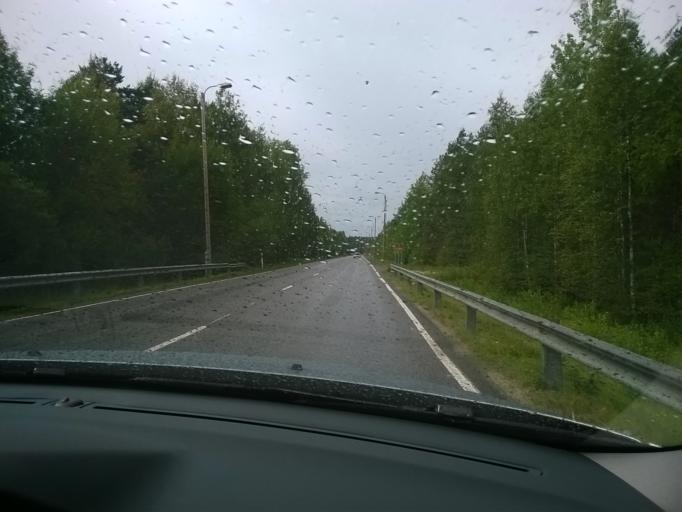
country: FI
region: Kainuu
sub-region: Kehys-Kainuu
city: Kuhmo
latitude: 64.1191
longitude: 29.5657
